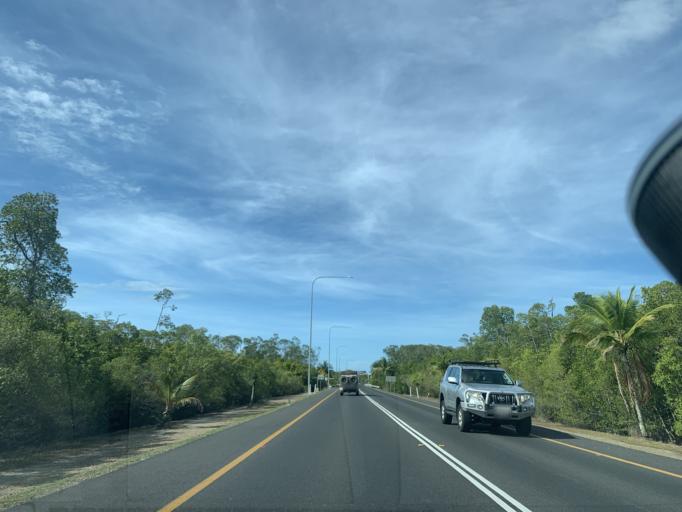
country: AU
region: Queensland
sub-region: Cairns
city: Cairns
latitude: -16.8932
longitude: 145.7603
